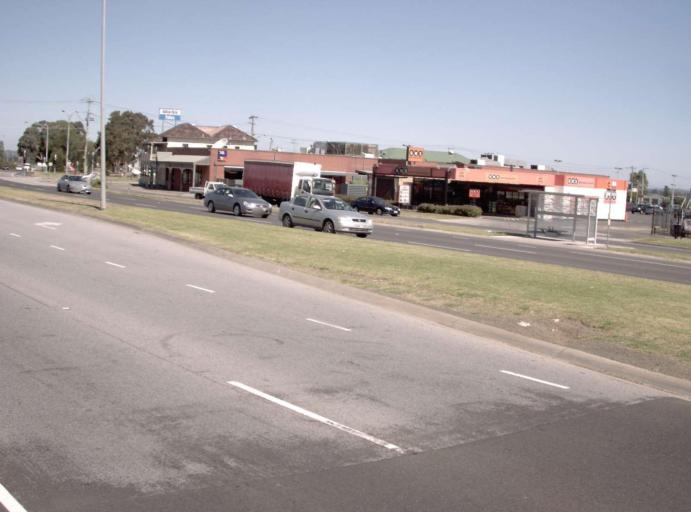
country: AU
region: Victoria
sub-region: Casey
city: Hallam
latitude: -38.0059
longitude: 145.2721
